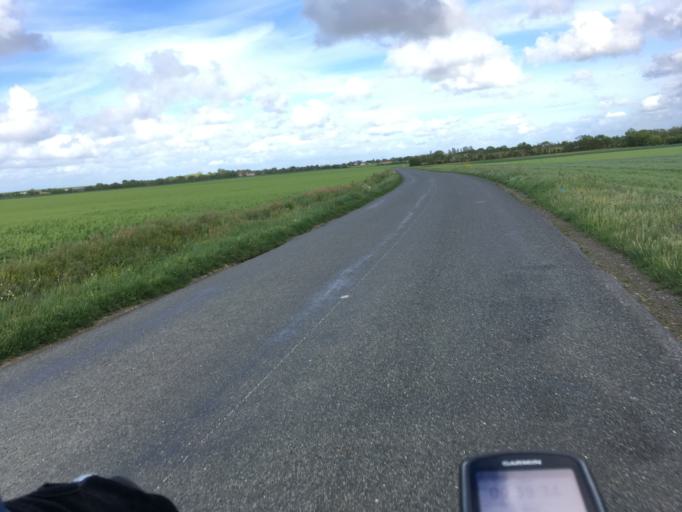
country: FR
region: Poitou-Charentes
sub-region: Departement de la Charente-Maritime
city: Verines
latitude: 46.1760
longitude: -0.9712
